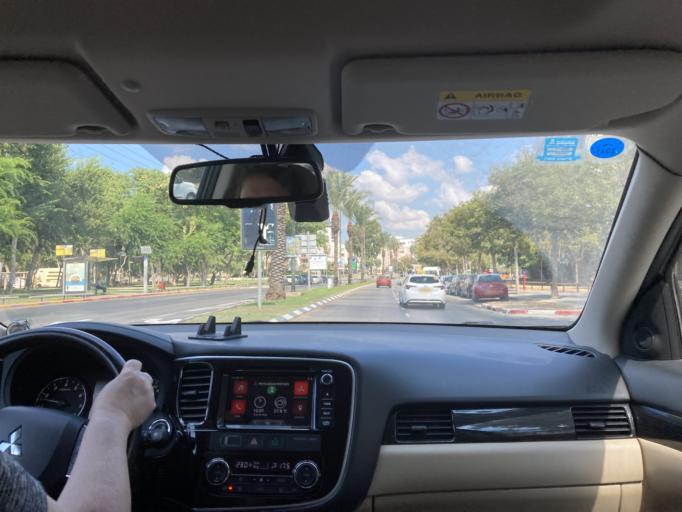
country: IL
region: Tel Aviv
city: Bene Beraq
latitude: 32.1126
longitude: 34.8395
